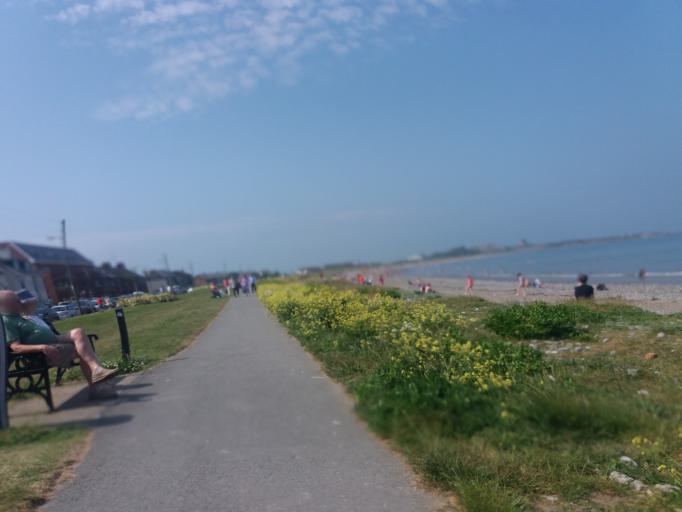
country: IE
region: Leinster
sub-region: Fingal County
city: Skerries
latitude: 53.5766
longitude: -6.1034
